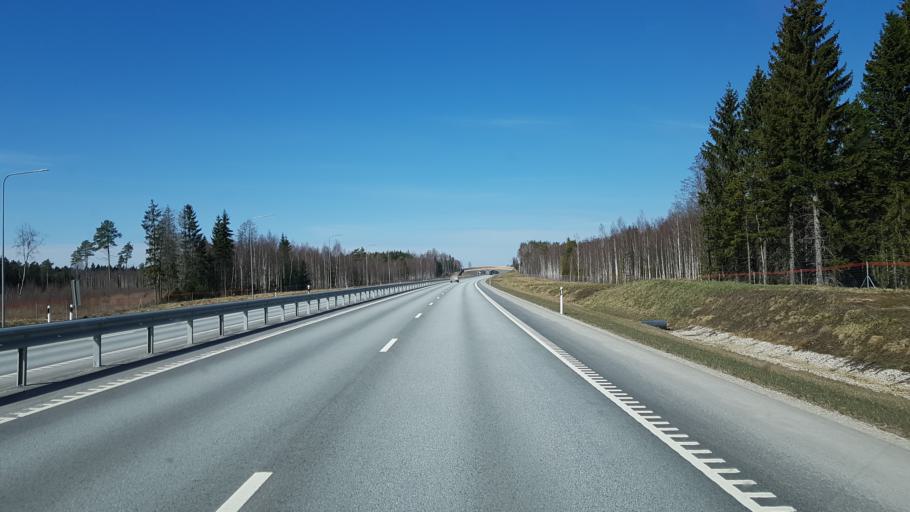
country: EE
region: Jaervamaa
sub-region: Paide linn
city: Paide
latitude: 59.0643
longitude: 25.3748
